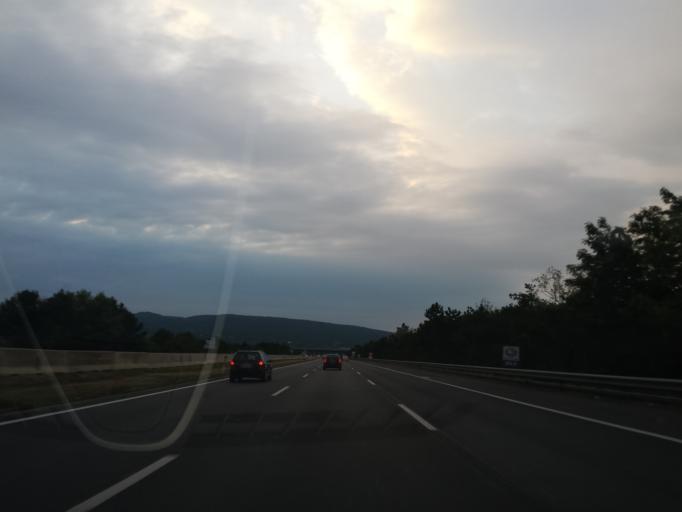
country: AT
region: Lower Austria
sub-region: Politischer Bezirk Wiener Neustadt
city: Weikersdorf am Steinfelde
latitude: 47.8136
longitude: 16.1945
